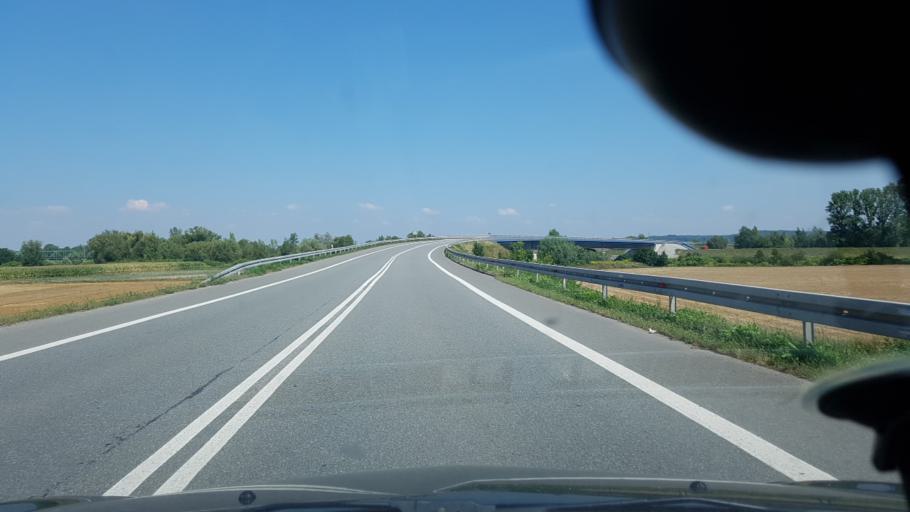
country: PL
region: Silesian Voivodeship
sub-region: Powiat wodzislawski
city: Olza
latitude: 49.9502
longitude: 18.3278
